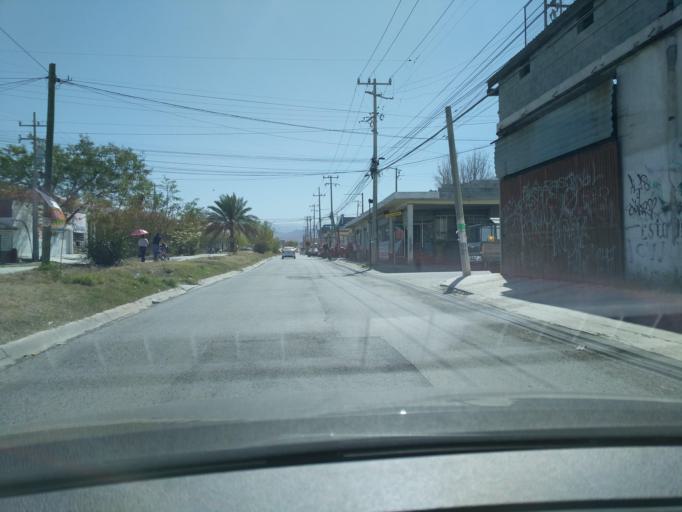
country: MX
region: Nuevo Leon
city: Juarez
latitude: 25.6365
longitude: -100.0865
